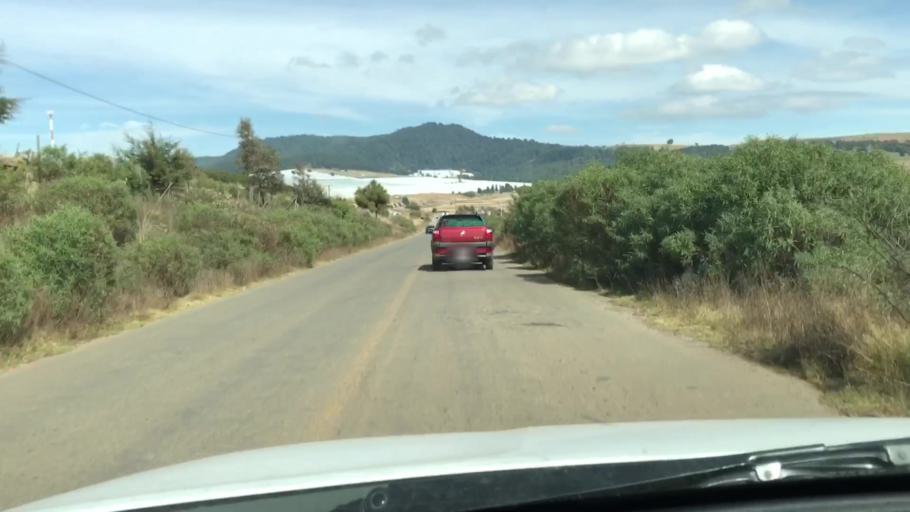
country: MX
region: Jalisco
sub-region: Amacueca
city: Tepec
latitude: 20.0172
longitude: -103.6923
